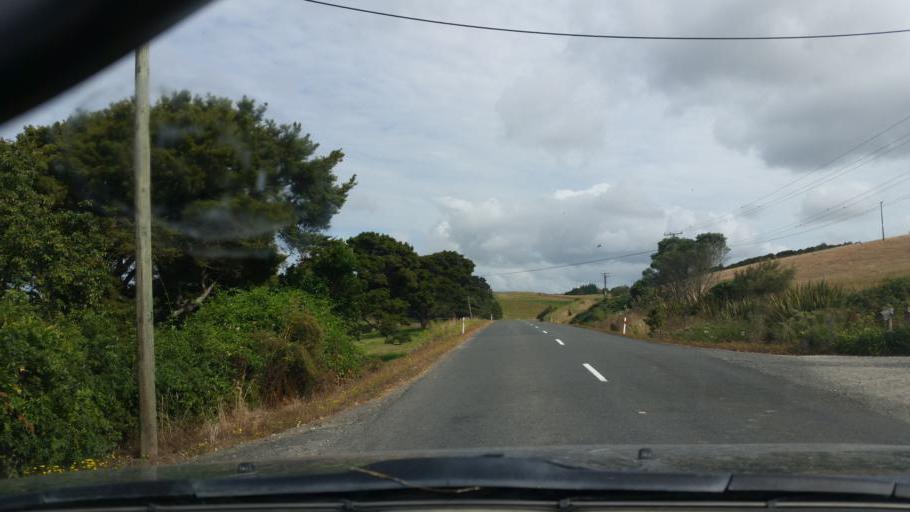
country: NZ
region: Northland
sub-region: Kaipara District
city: Dargaville
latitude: -35.9629
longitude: 173.9282
